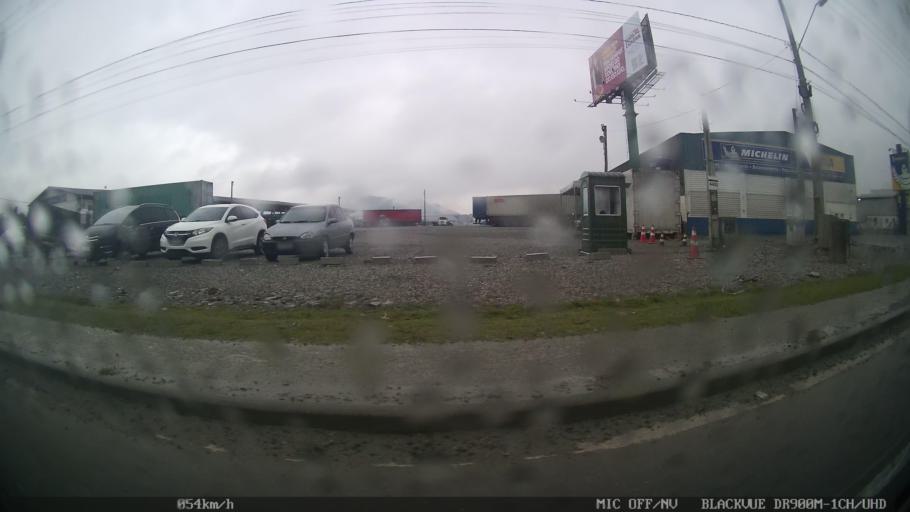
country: BR
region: Santa Catarina
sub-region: Itajai
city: Itajai
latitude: -26.8812
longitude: -48.7252
